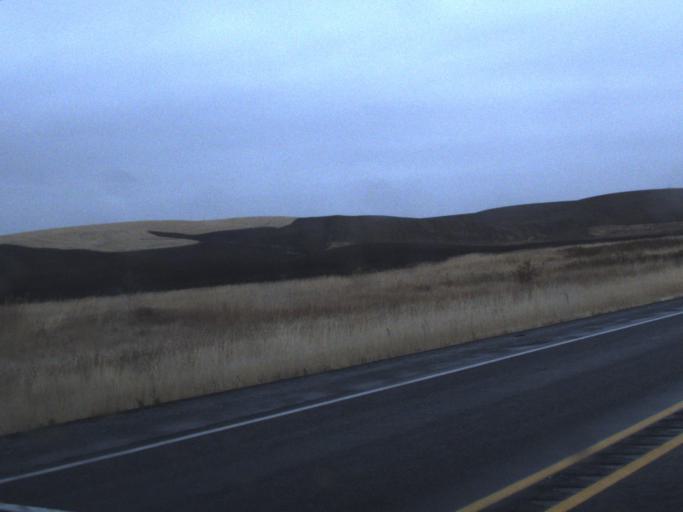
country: US
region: Washington
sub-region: Whitman County
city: Colfax
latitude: 46.9608
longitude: -117.3303
